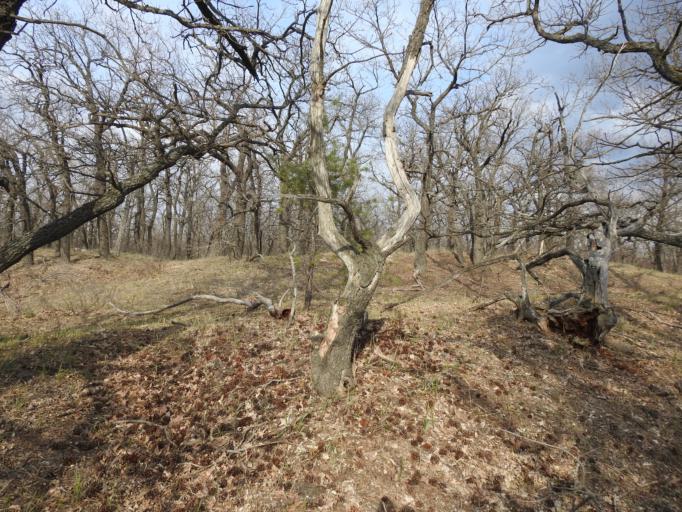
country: RU
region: Saratov
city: Krasnyy Oktyabr'
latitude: 51.4276
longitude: 45.5426
